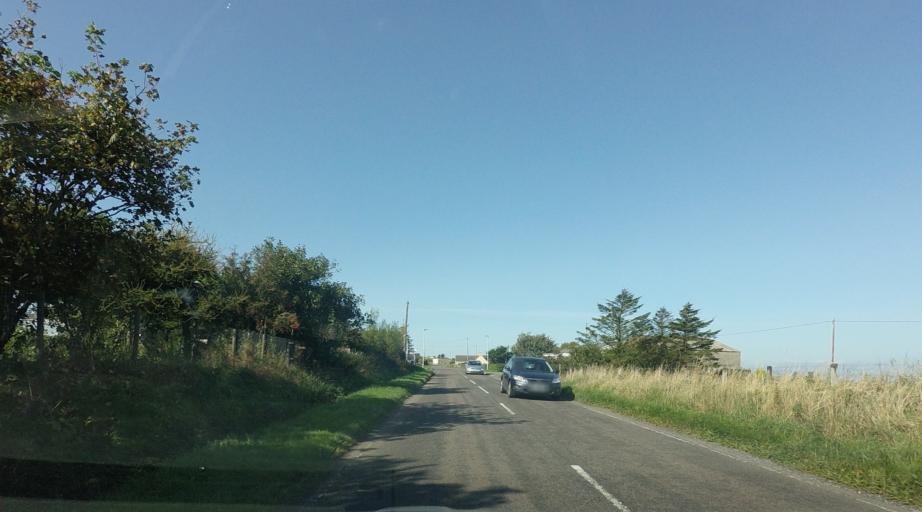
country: GB
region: Scotland
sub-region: Highland
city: Wick
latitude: 58.6380
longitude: -3.1686
